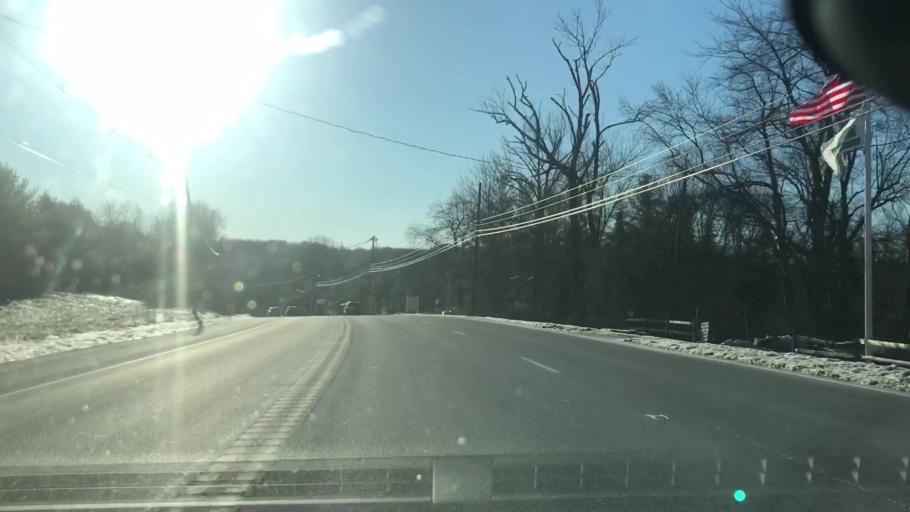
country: US
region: New Jersey
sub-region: Morris County
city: Chester
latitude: 40.8024
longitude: -74.7137
